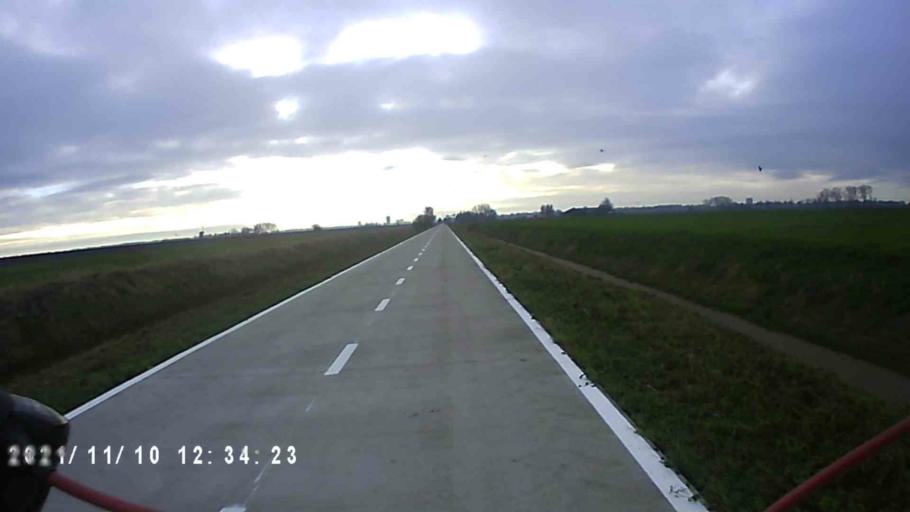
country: NL
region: Groningen
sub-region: Gemeente Groningen
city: Korrewegwijk
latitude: 53.2699
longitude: 6.5432
